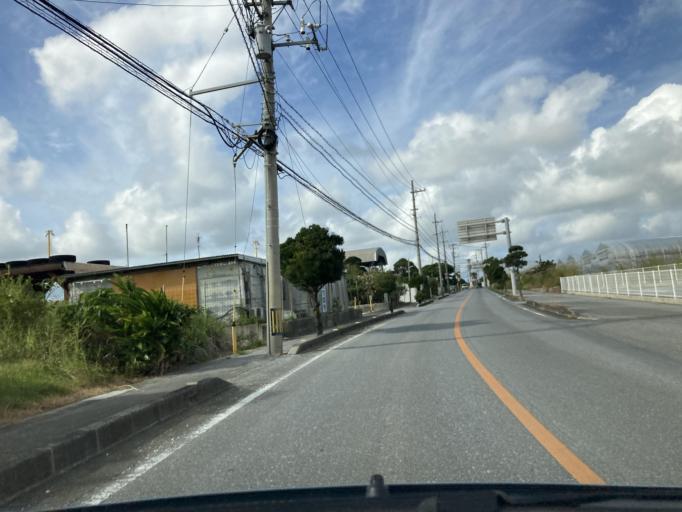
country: JP
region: Okinawa
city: Itoman
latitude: 26.1085
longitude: 127.7203
